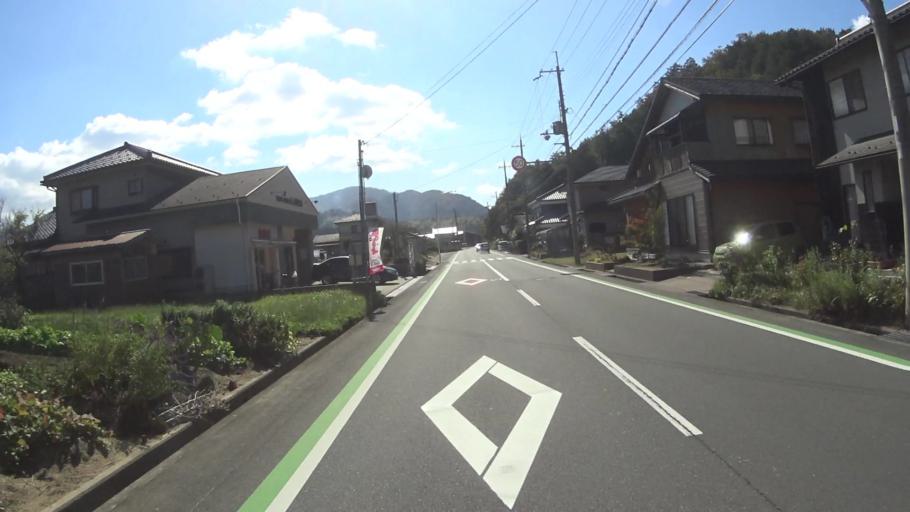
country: JP
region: Kyoto
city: Miyazu
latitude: 35.6559
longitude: 135.0891
